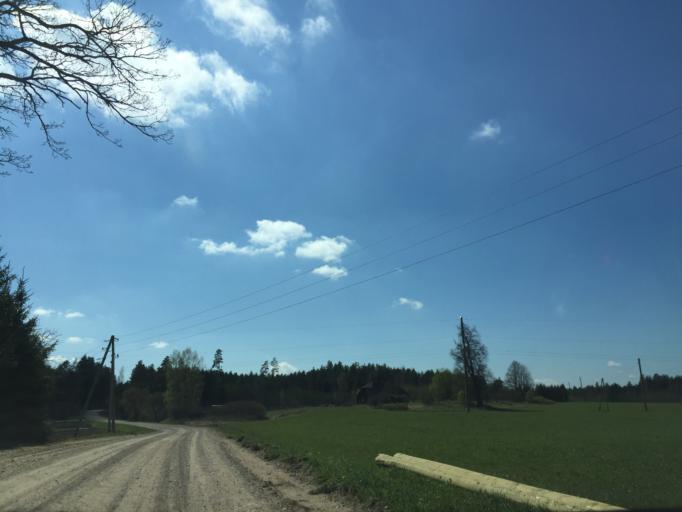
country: LV
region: Smiltene
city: Smiltene
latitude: 57.5829
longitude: 25.9417
